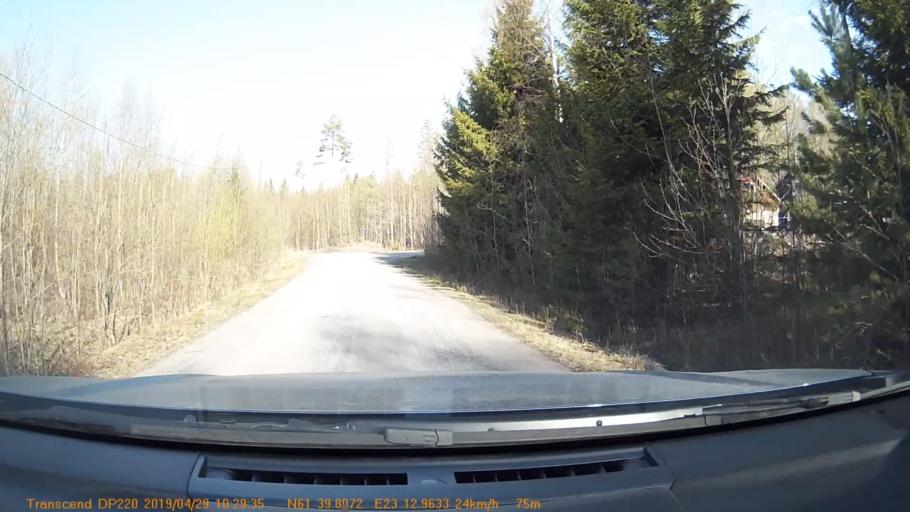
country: FI
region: Pirkanmaa
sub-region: Tampere
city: Haemeenkyroe
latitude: 61.6636
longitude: 23.2158
